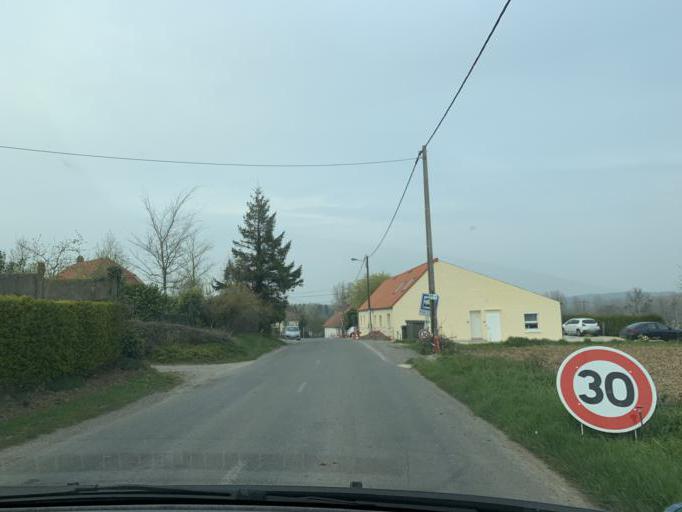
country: FR
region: Nord-Pas-de-Calais
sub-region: Departement du Pas-de-Calais
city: Samer
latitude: 50.6811
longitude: 1.7595
